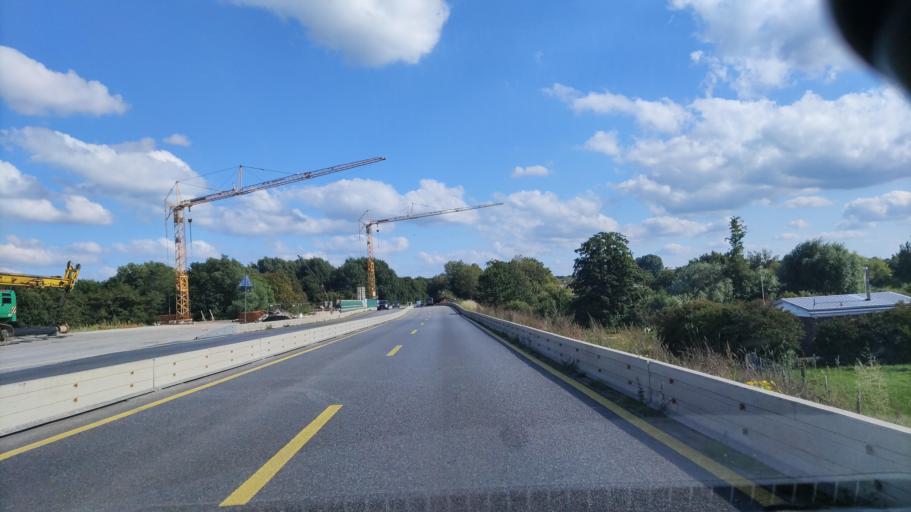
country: DE
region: Schleswig-Holstein
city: Westerronfeld
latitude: 54.3011
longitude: 9.6456
